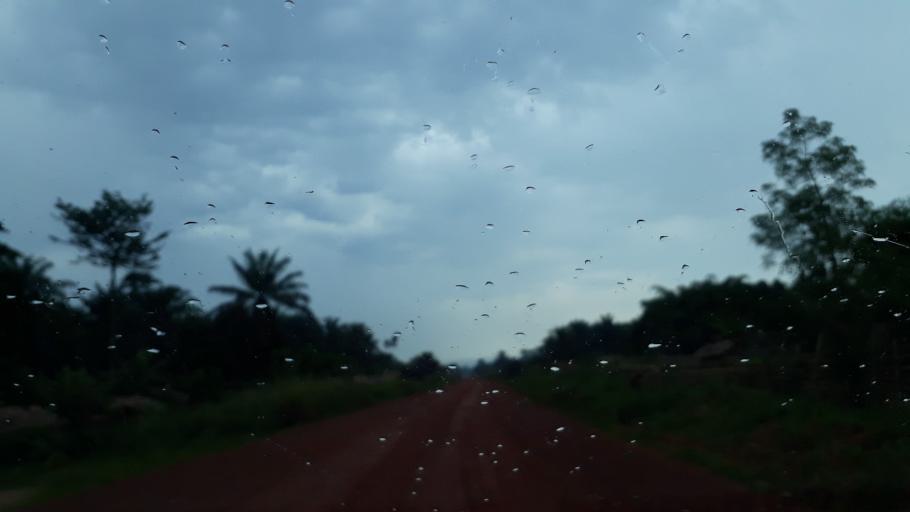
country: CD
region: Eastern Province
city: Kisangani
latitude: 0.4660
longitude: 25.4201
